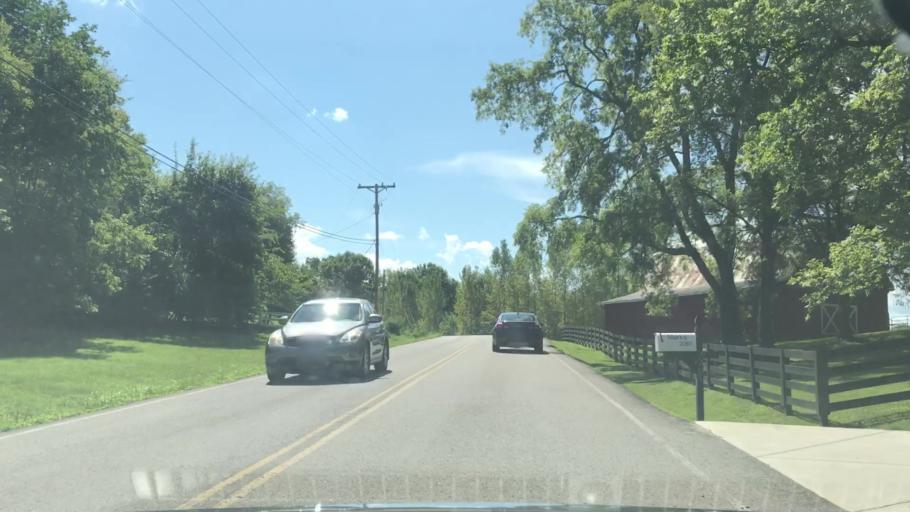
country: US
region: Tennessee
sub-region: Williamson County
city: Franklin
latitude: 35.9566
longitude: -86.8490
